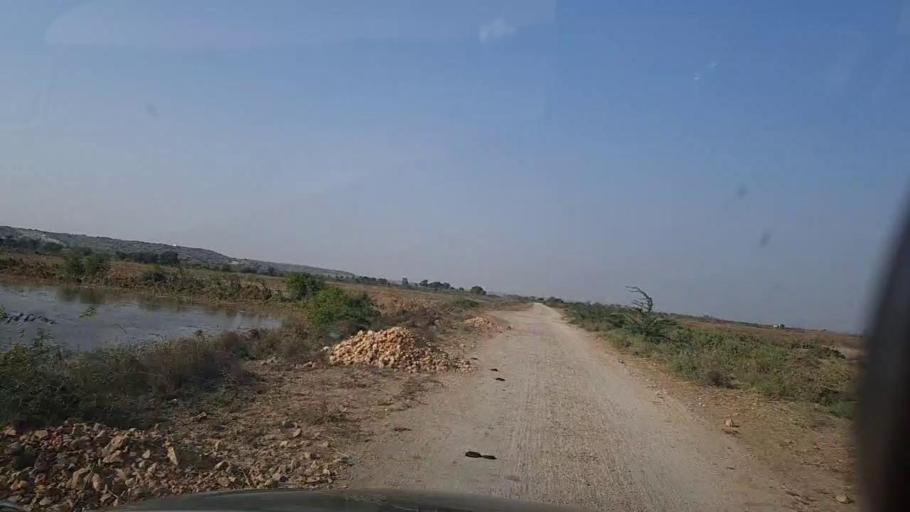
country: PK
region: Sindh
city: Thatta
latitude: 24.5897
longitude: 67.8763
